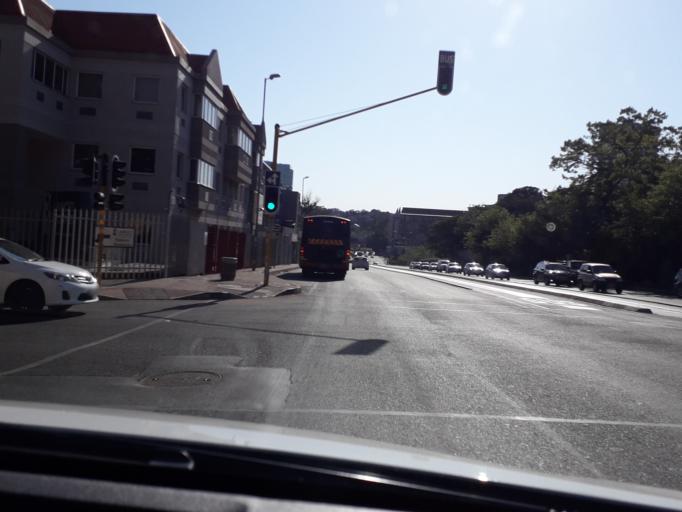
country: ZA
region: Gauteng
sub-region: City of Johannesburg Metropolitan Municipality
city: Johannesburg
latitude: -26.1838
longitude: 28.0141
